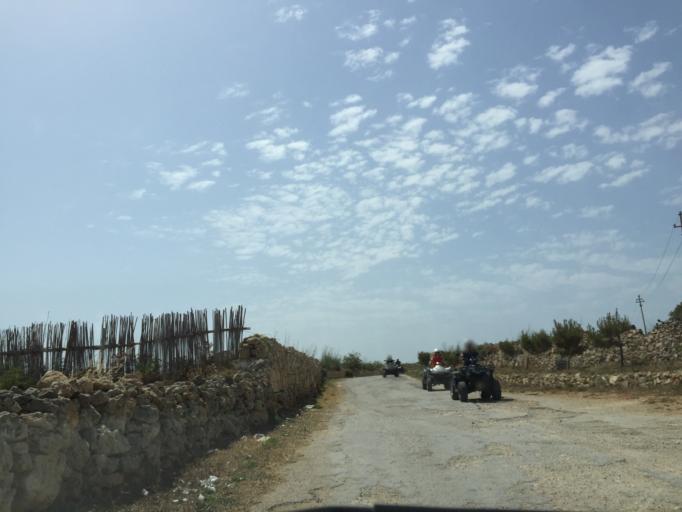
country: MT
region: In-Nadur
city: Nadur
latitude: 36.0550
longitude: 14.2941
